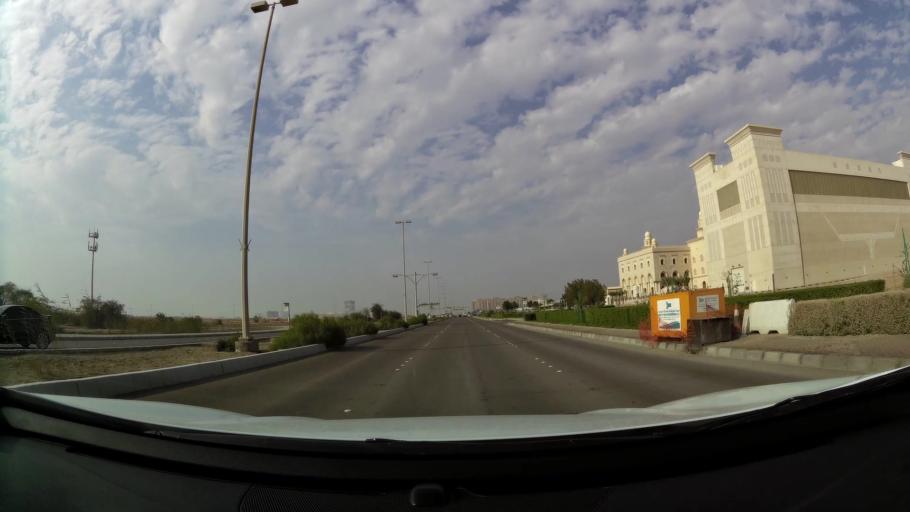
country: AE
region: Abu Dhabi
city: Abu Dhabi
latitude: 24.3577
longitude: 54.5372
